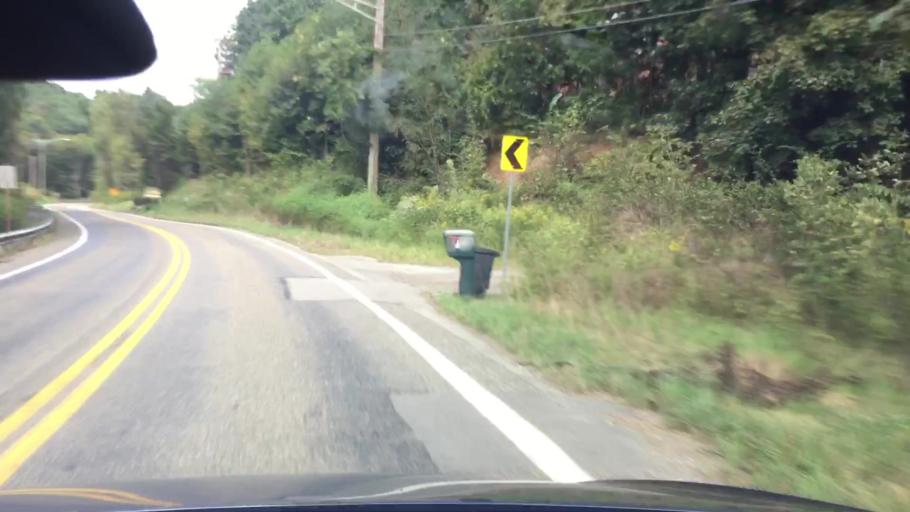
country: US
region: Pennsylvania
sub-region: Allegheny County
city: Cheswick
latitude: 40.5635
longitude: -79.8197
